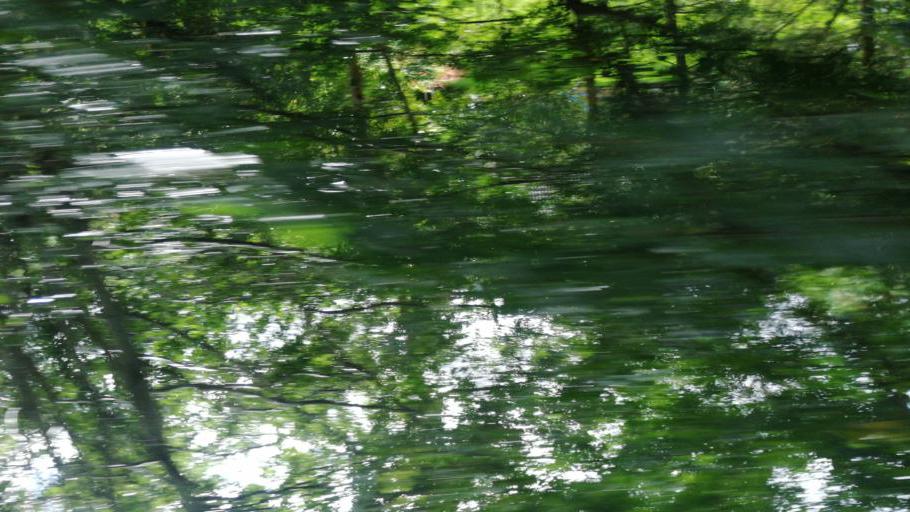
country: GB
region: Scotland
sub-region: Aberdeenshire
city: Insch
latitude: 57.3222
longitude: -2.5464
